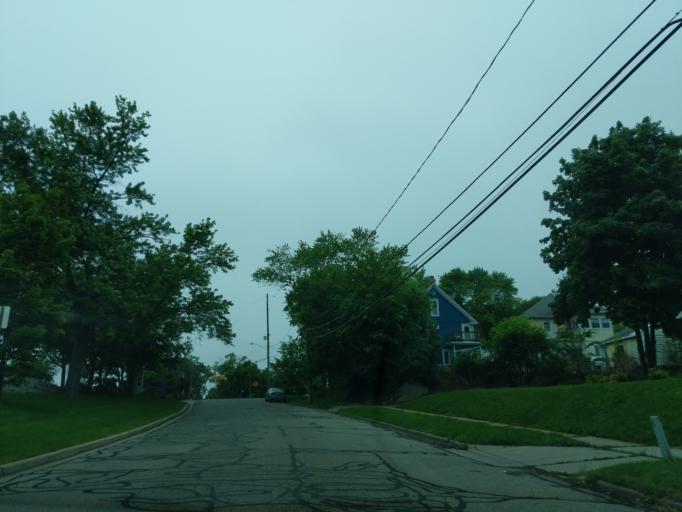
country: US
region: Michigan
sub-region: Jackson County
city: Jackson
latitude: 42.2526
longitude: -84.3930
